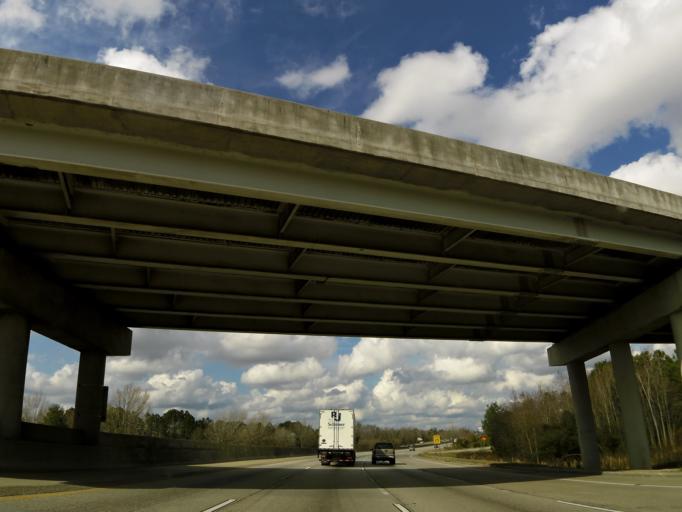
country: US
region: South Carolina
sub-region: Berkeley County
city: Hanahan
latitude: 32.8832
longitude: -80.0197
